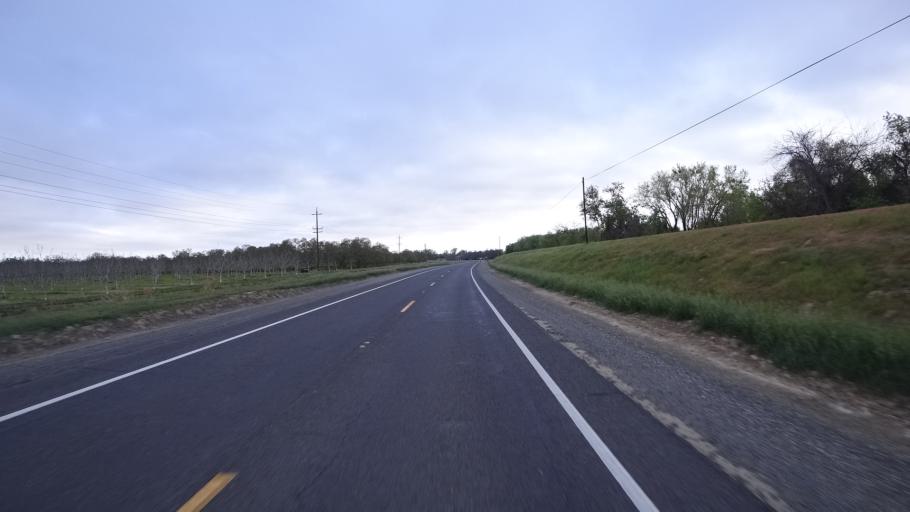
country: US
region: California
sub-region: Glenn County
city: Willows
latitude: 39.4324
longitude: -122.0111
